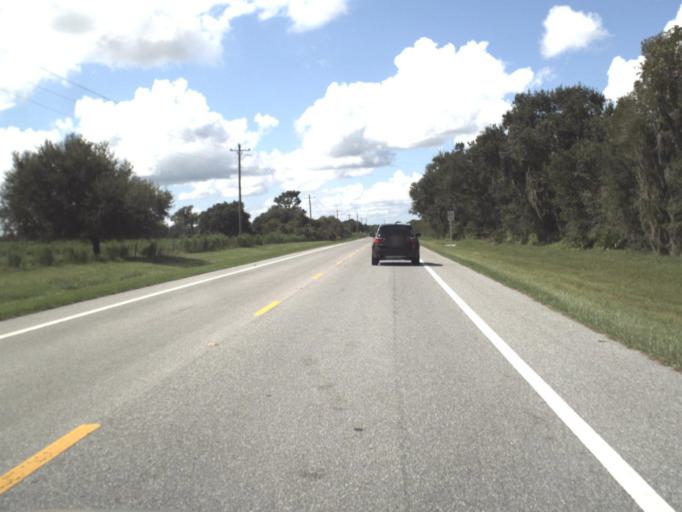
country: US
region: Florida
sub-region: DeSoto County
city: Arcadia
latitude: 27.3085
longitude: -82.0959
